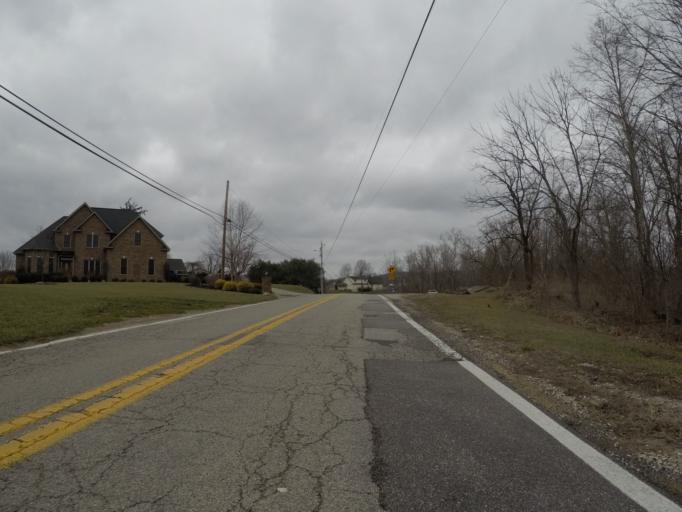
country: US
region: West Virginia
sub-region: Cabell County
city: Barboursville
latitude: 38.4275
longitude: -82.2406
